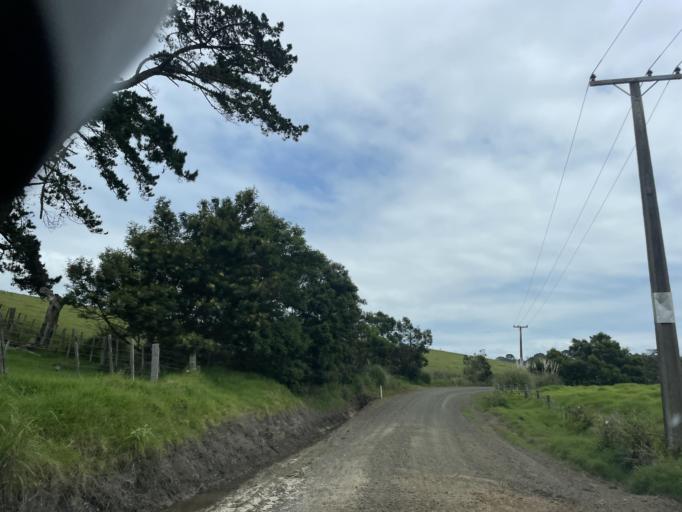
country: NZ
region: Auckland
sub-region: Auckland
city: Wellsford
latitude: -36.2549
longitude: 174.2360
